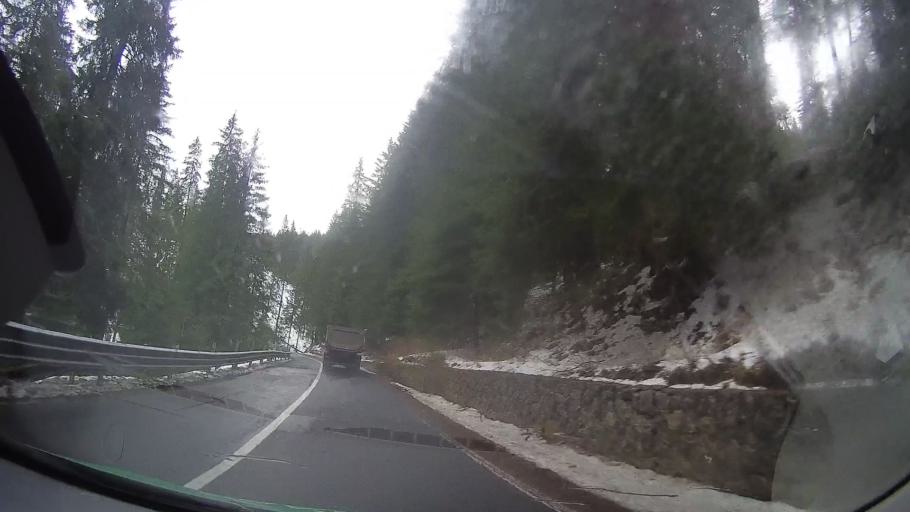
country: RO
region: Harghita
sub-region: Municipiul Gheorgheni
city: Gheorgheni
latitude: 46.7789
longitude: 25.7294
